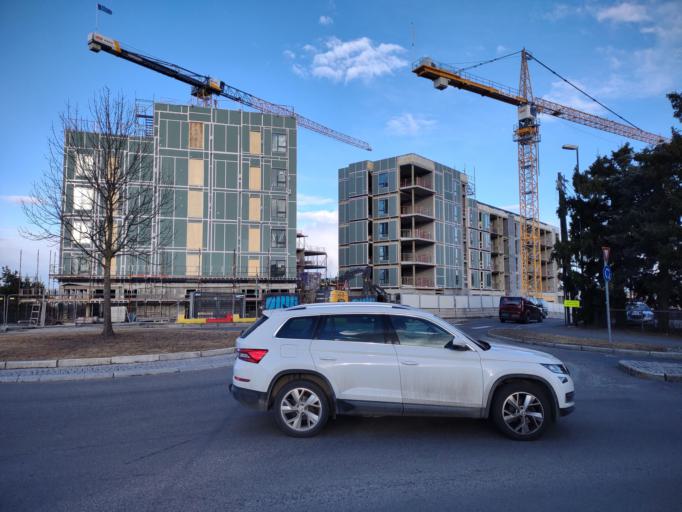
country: NO
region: Akershus
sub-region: Skedsmo
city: Lillestrom
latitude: 59.9621
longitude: 11.0088
